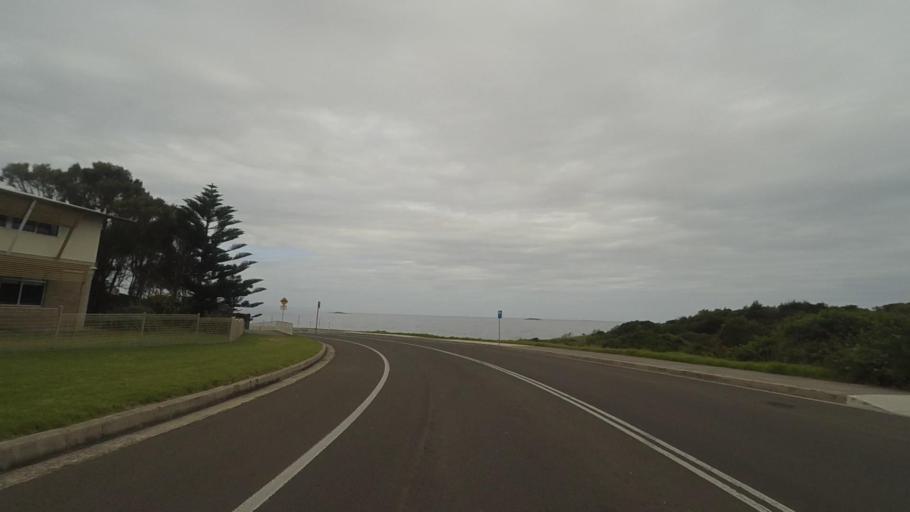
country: AU
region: New South Wales
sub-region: Wollongong
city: Port Kembla
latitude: -34.4871
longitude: 150.9151
